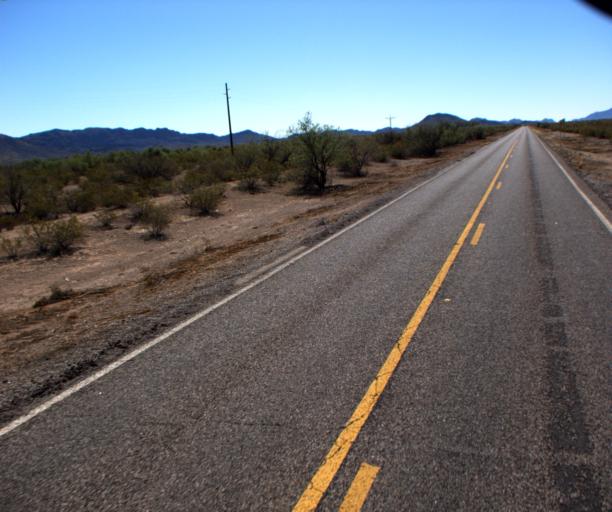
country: US
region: Arizona
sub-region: Pima County
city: Ajo
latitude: 32.3215
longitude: -112.7708
